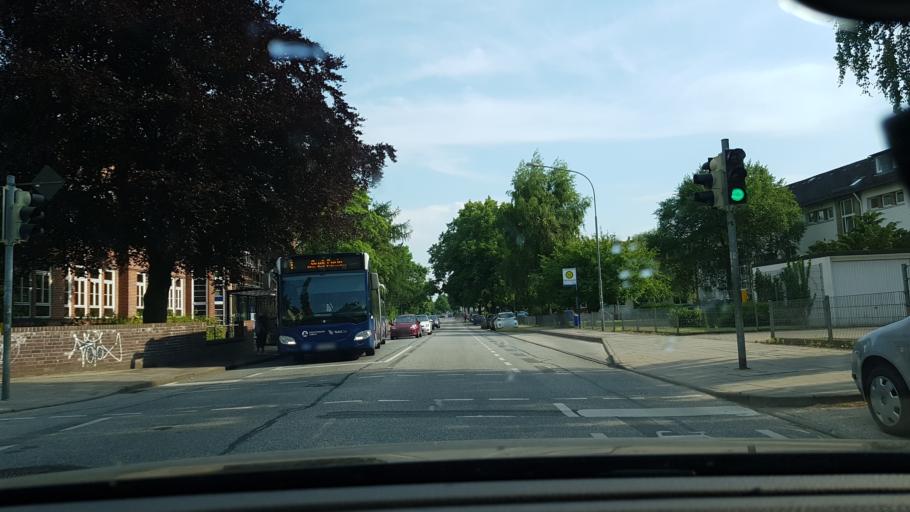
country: DE
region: Schleswig-Holstein
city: Luebeck
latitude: 53.8481
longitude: 10.6989
